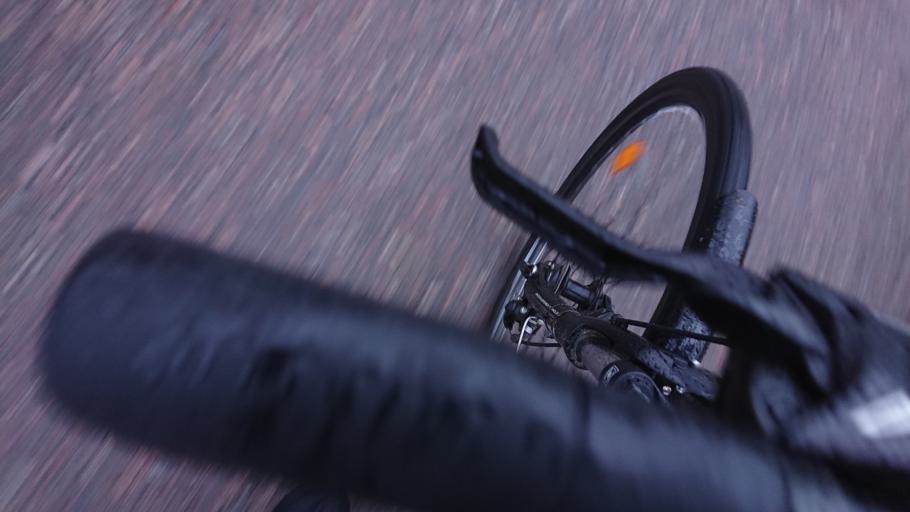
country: FI
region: Pirkanmaa
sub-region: Tampere
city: Tampere
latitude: 61.4547
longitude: 23.8722
